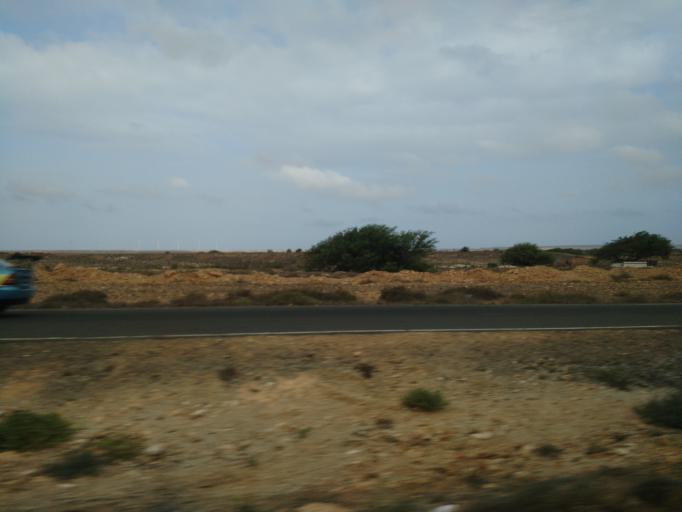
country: CV
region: Sal
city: Espargos
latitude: 16.7010
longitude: -22.9408
